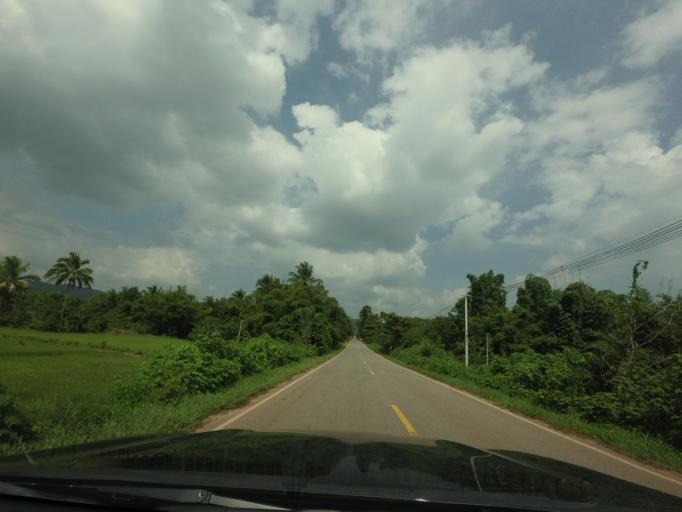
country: TH
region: Uttaradit
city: Ban Khok
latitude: 18.0374
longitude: 101.0978
